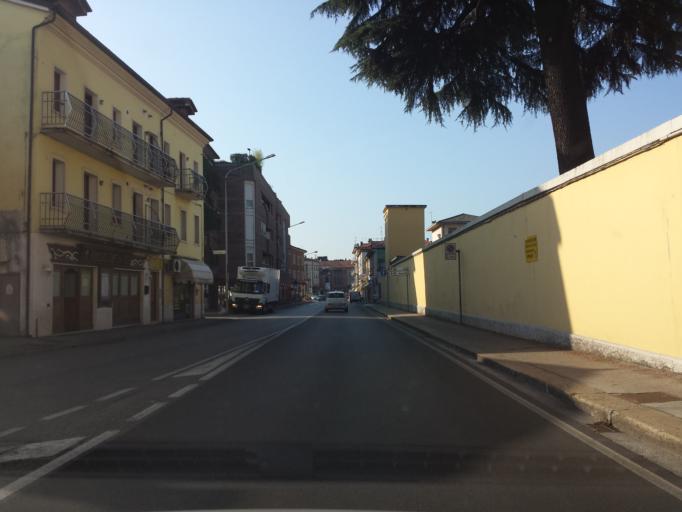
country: IT
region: Veneto
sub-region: Provincia di Vicenza
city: Vicenza
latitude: 45.5608
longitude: 11.5443
